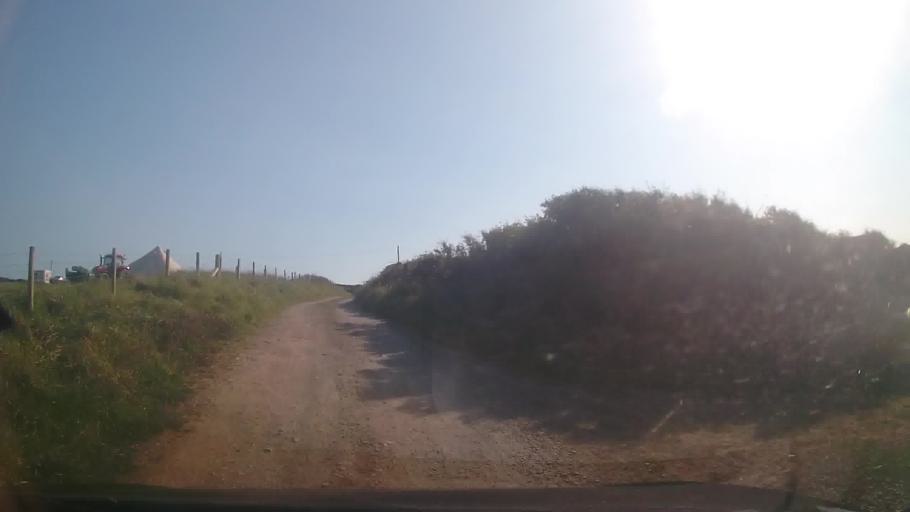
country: GB
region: Wales
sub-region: Pembrokeshire
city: Llanrhian
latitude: 51.9270
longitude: -5.2196
